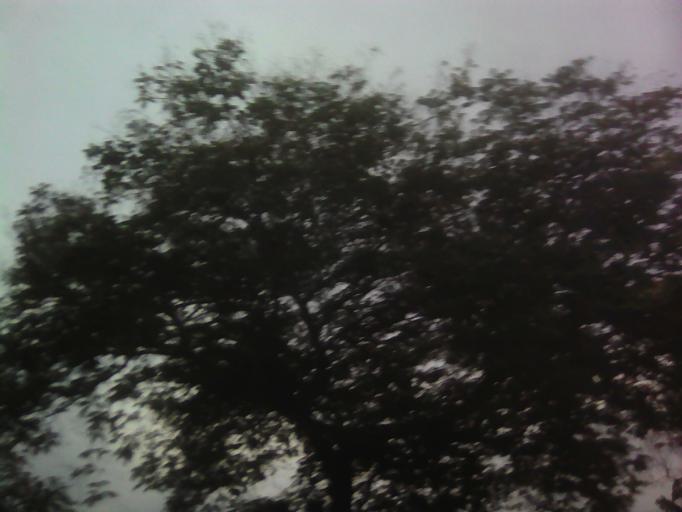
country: MY
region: Penang
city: Perai
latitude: 5.3976
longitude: 100.4217
